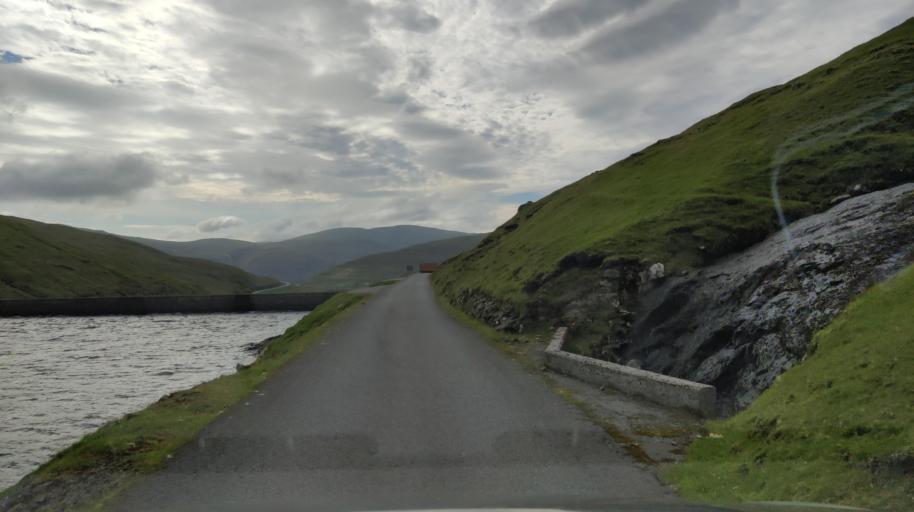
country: FO
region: Streymoy
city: Vestmanna
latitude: 62.1541
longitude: -7.1280
